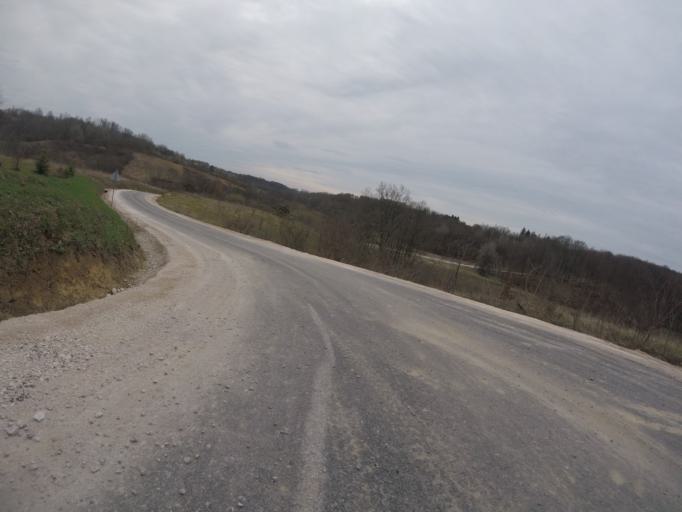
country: HR
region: Grad Zagreb
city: Strmec
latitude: 45.6056
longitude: 15.9099
